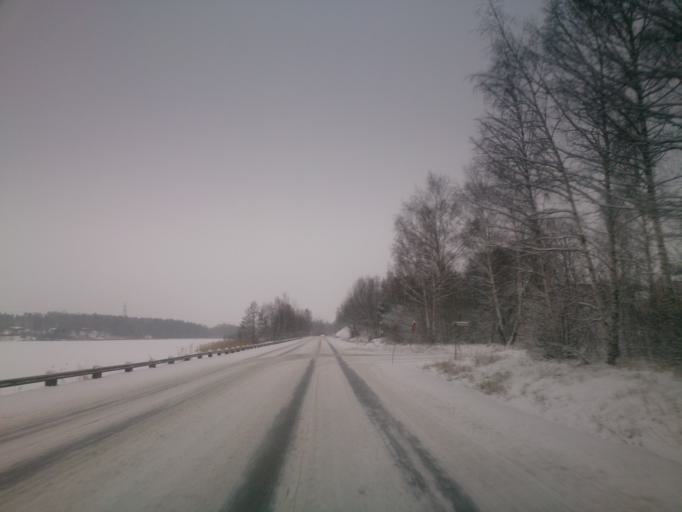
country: SE
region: OEstergoetland
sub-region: Norrkopings Kommun
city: Skarblacka
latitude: 58.5887
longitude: 15.8717
